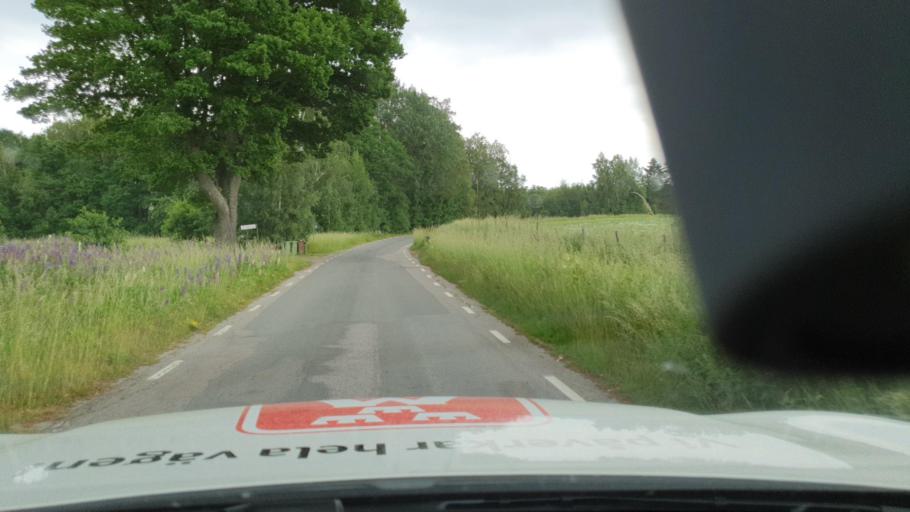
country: SE
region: Vaestra Goetaland
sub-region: Hjo Kommun
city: Hjo
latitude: 58.1747
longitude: 14.1937
